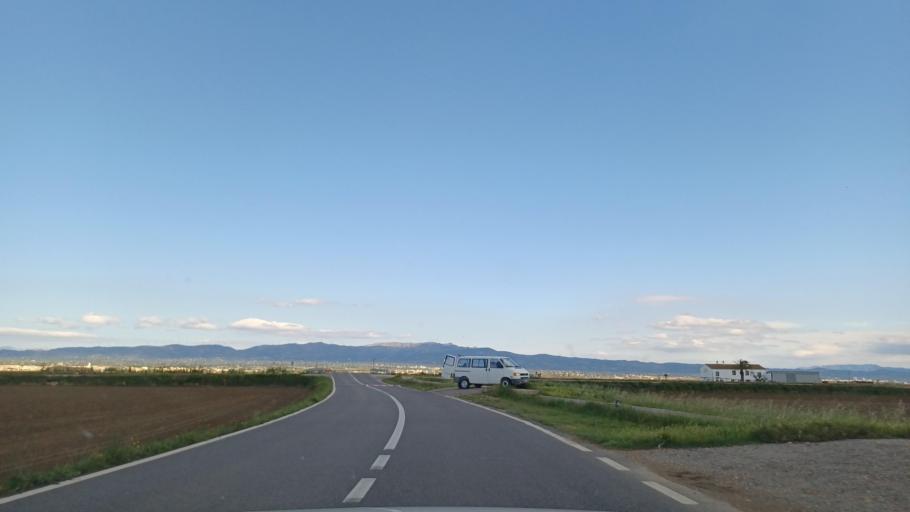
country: ES
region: Catalonia
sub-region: Provincia de Tarragona
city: Deltebre
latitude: 40.7533
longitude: 0.7044
